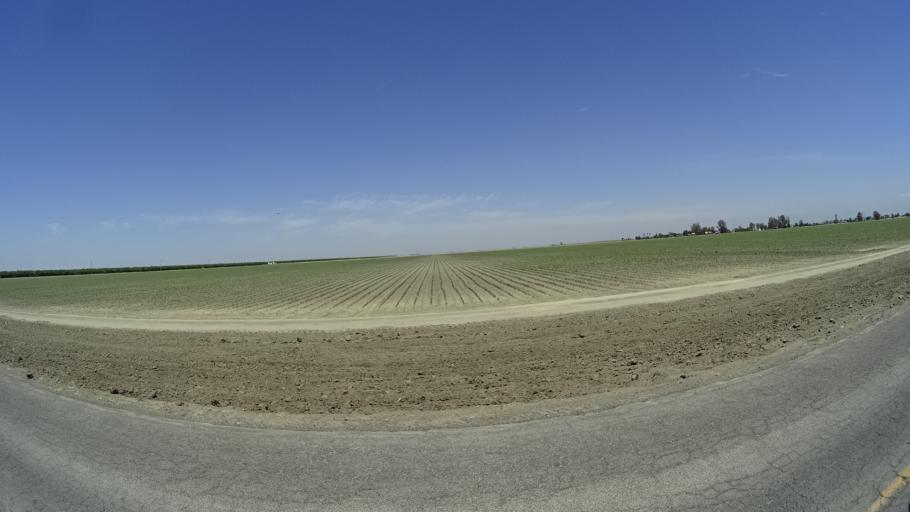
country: US
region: California
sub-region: Kings County
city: Corcoran
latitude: 36.1092
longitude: -119.5873
